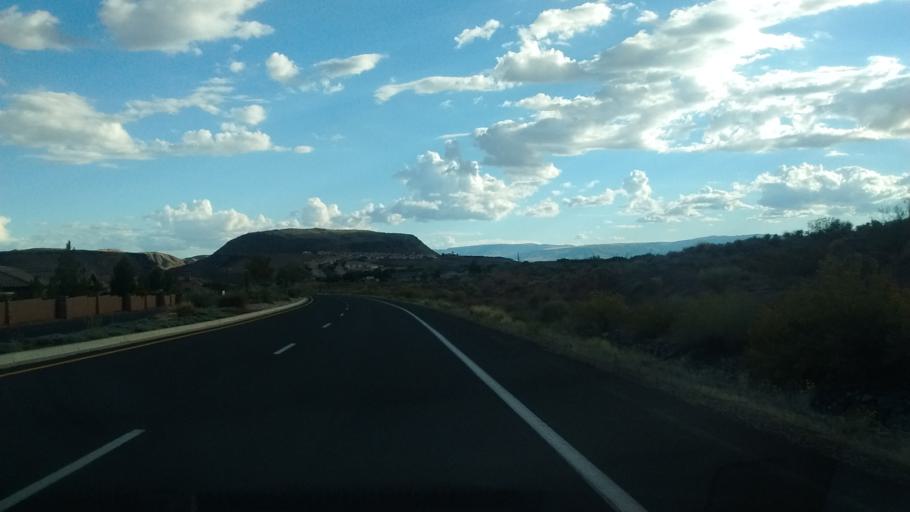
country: US
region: Utah
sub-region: Washington County
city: Washington
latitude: 37.1403
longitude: -113.4856
